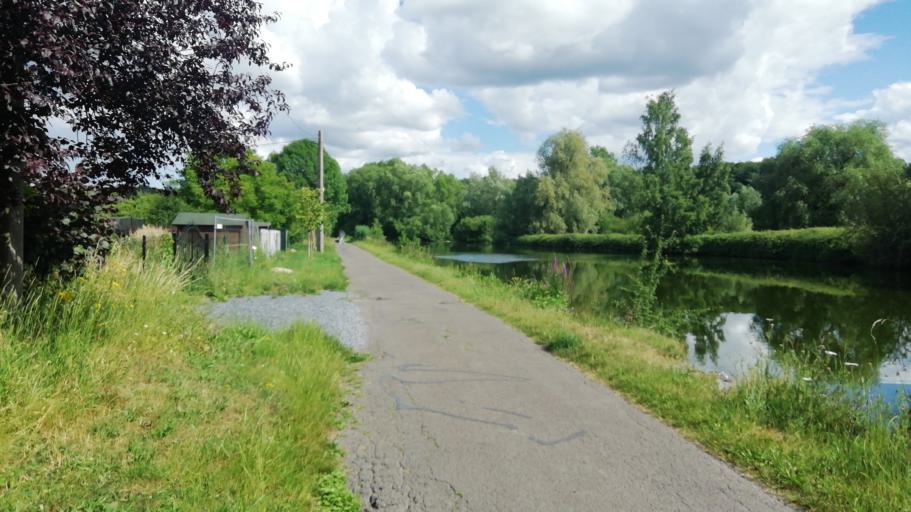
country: BE
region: Wallonia
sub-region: Province du Hainaut
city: Merbes-le-Chateau
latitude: 50.3150
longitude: 4.1843
